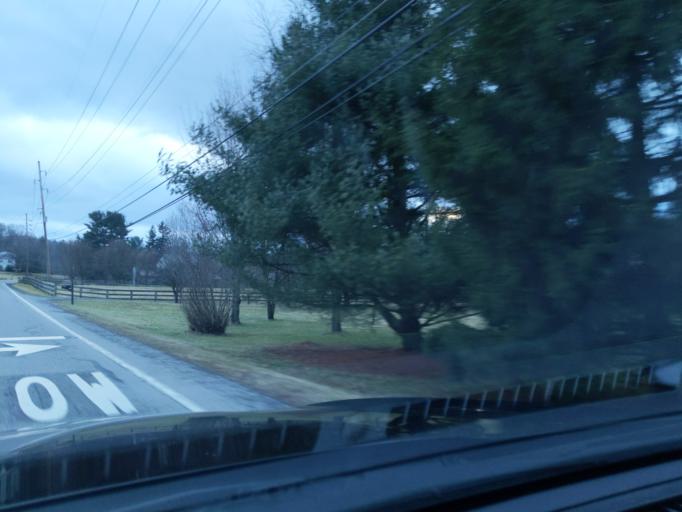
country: US
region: Pennsylvania
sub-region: Blair County
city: Bellwood
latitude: 40.5876
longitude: -78.3388
